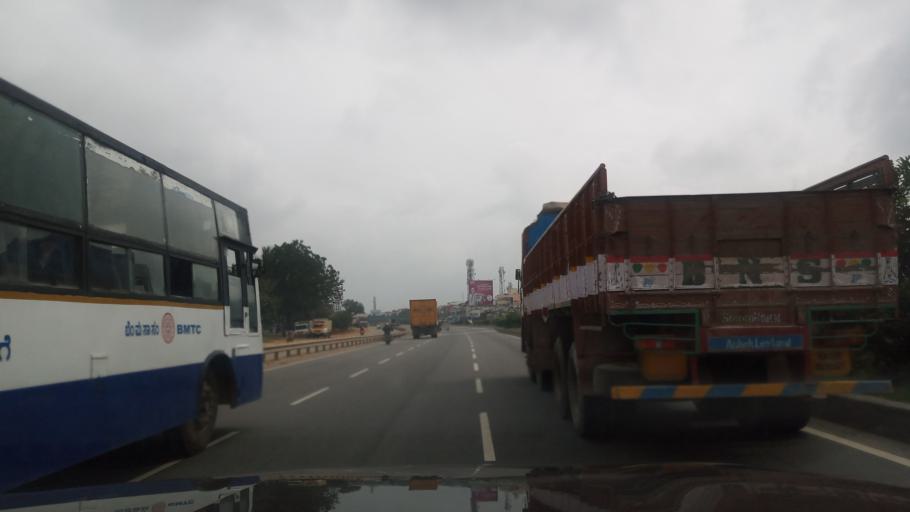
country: IN
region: Karnataka
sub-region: Bangalore Urban
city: Anekal
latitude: 12.7899
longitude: 77.7333
